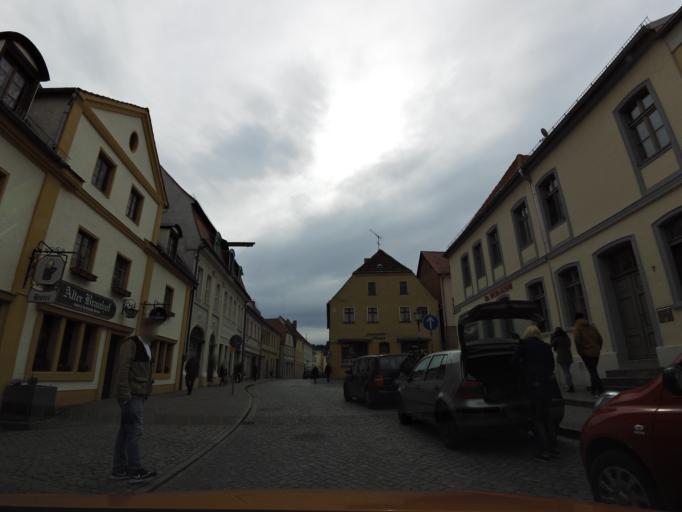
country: DE
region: Brandenburg
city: Belzig
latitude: 52.1406
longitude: 12.5879
